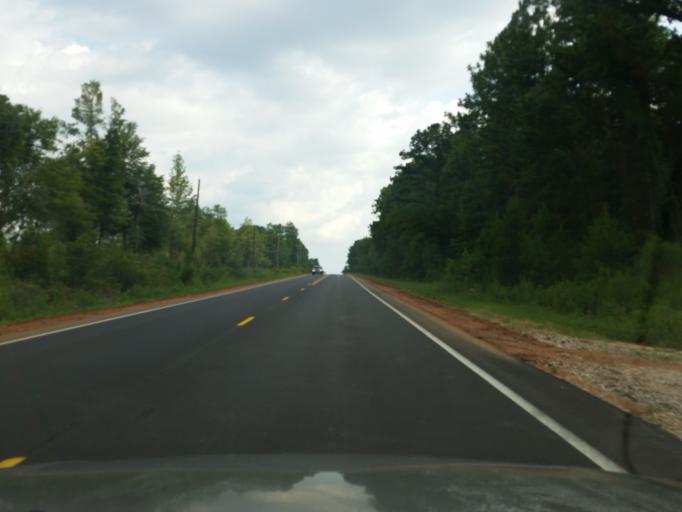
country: US
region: Alabama
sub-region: Baldwin County
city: Spanish Fort
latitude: 30.6953
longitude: -87.9023
